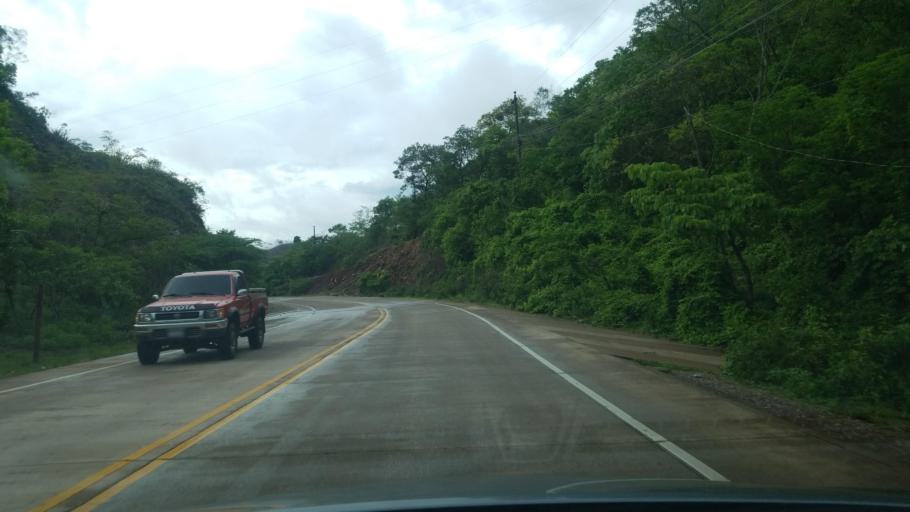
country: HN
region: Copan
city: Copan
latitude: 14.8541
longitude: -89.1987
